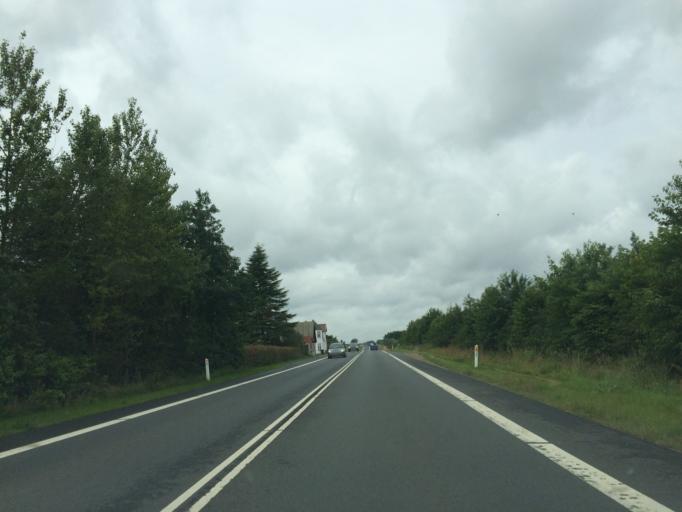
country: DK
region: Central Jutland
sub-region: Silkeborg Kommune
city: Svejbaek
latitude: 56.2159
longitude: 9.6179
